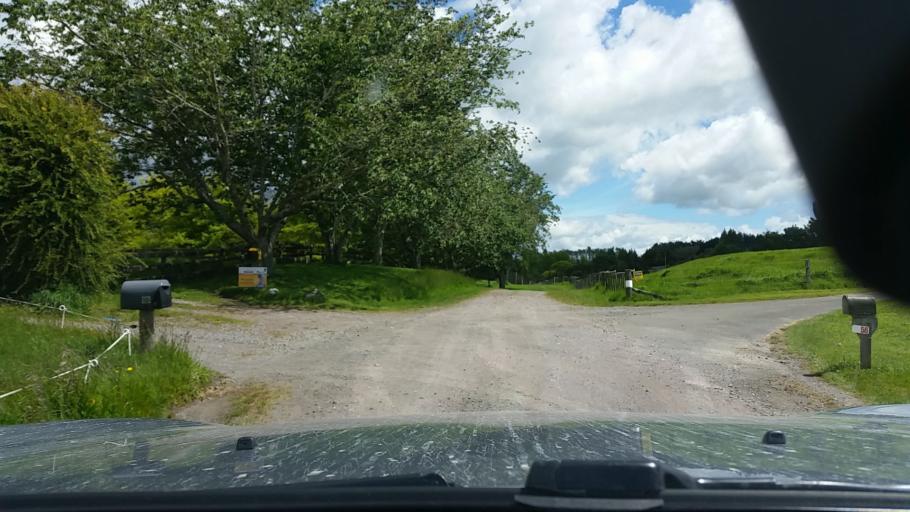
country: NZ
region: Bay of Plenty
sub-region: Rotorua District
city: Rotorua
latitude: -38.0382
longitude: 176.1935
